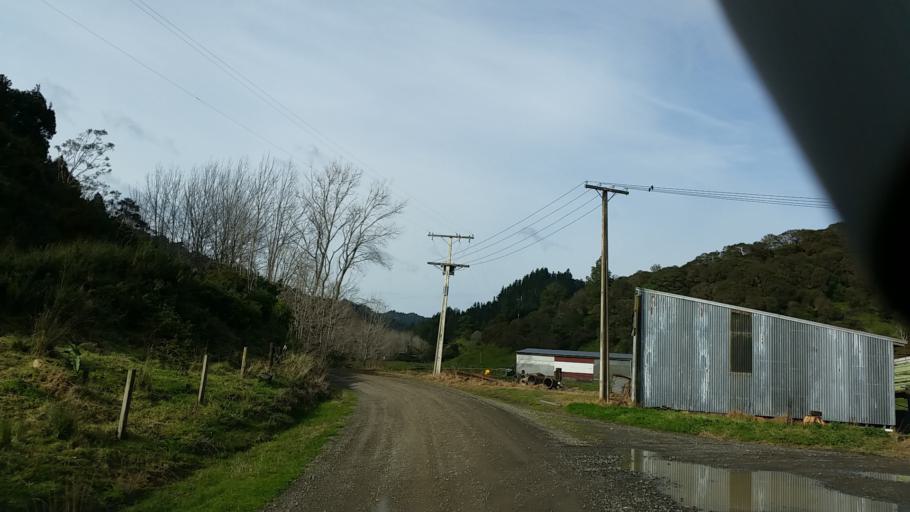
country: NZ
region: Taranaki
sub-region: New Plymouth District
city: Waitara
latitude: -39.0539
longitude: 174.4625
